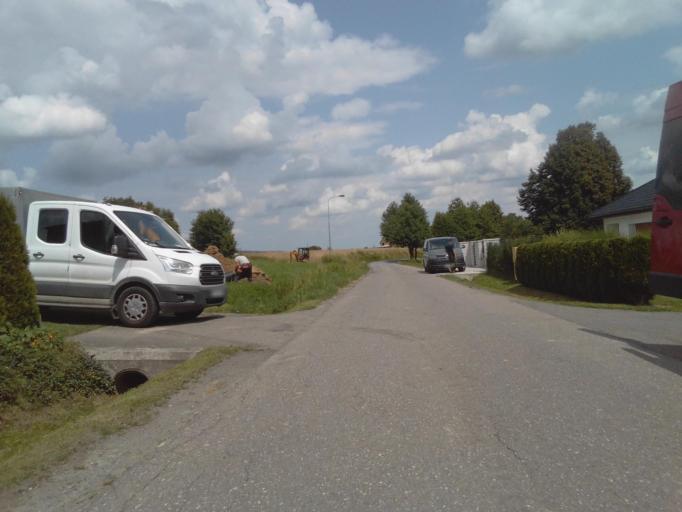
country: PL
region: Subcarpathian Voivodeship
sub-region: Powiat strzyzowski
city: Frysztak
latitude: 49.8248
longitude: 21.6001
